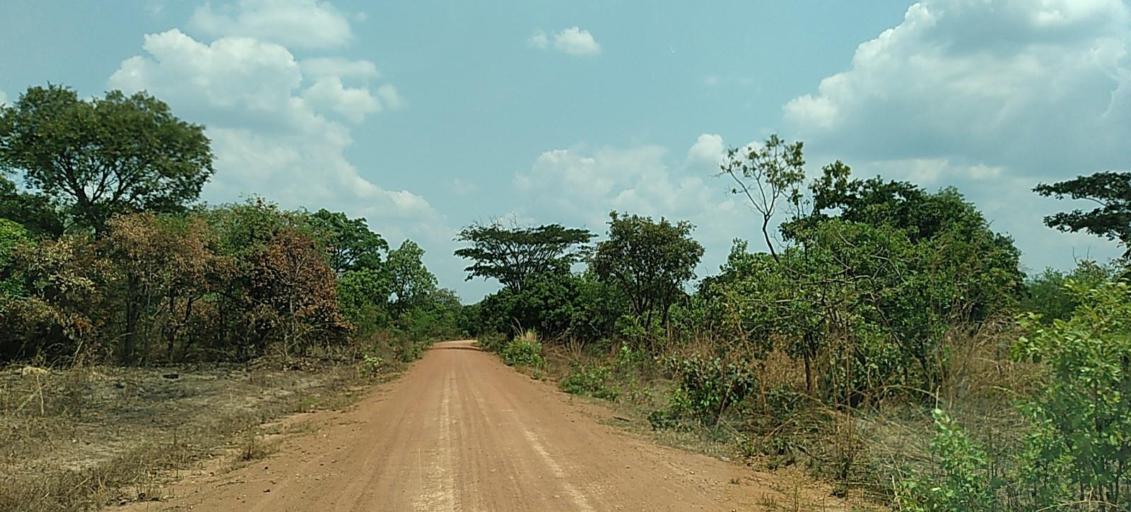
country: ZM
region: Copperbelt
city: Luanshya
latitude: -13.1435
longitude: 28.3166
